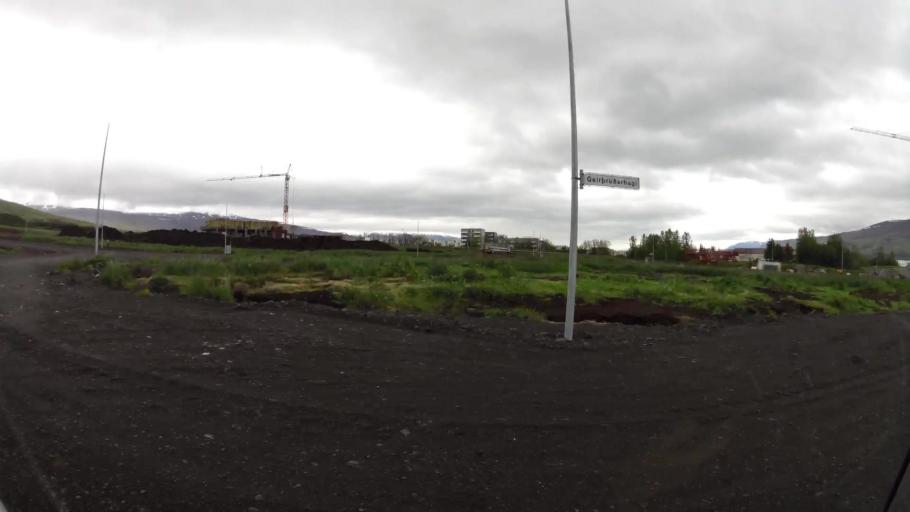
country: IS
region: Northeast
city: Akureyri
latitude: 65.6592
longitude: -18.0947
